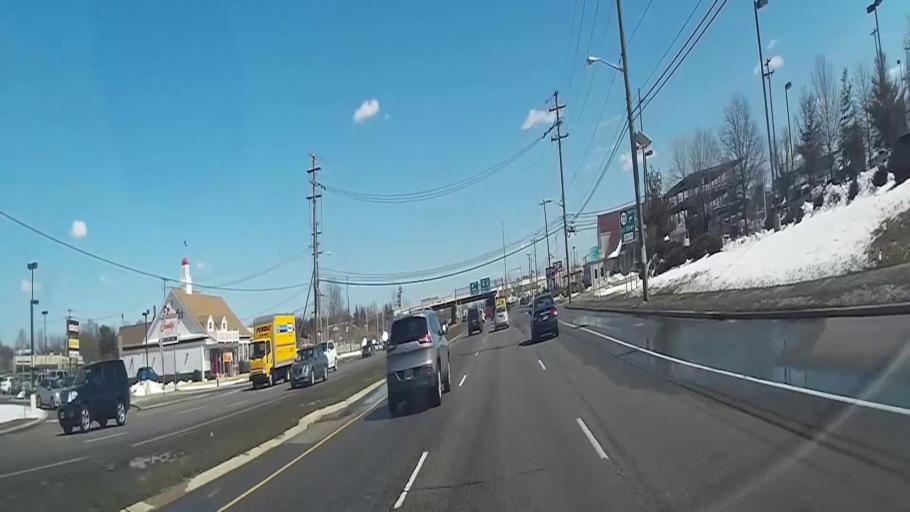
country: US
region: New Jersey
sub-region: Burlington County
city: Marlton
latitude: 39.8942
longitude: -74.9310
